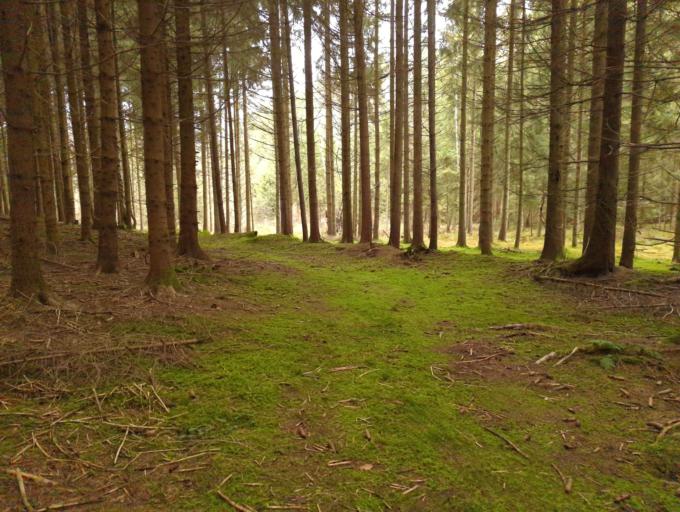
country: DE
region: Bavaria
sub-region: Swabia
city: Rettenbach
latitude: 48.4310
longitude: 10.3180
